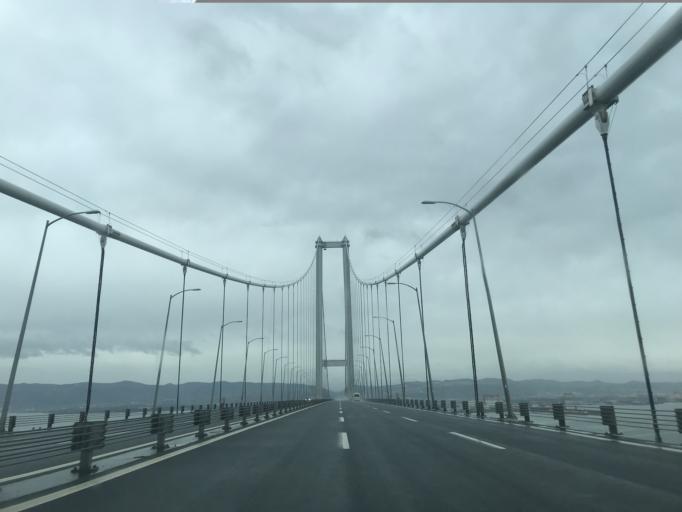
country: TR
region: Yalova
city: Altinova
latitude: 40.7535
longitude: 29.5157
